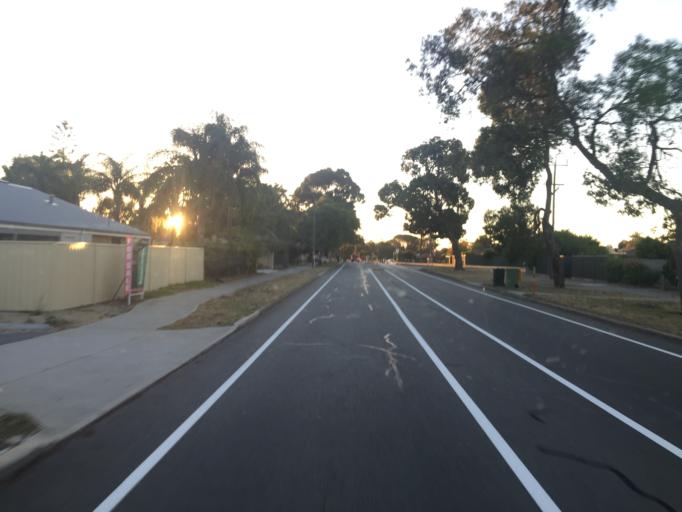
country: AU
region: Western Australia
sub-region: Gosnells
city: Maddington
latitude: -32.0330
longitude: 115.9842
